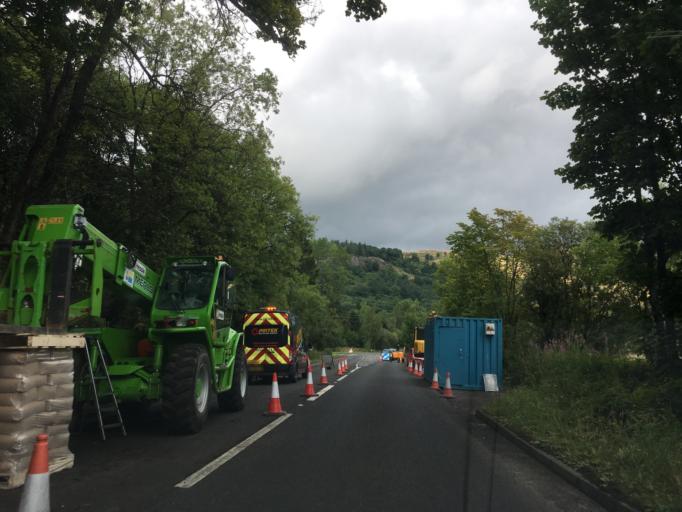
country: GB
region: Scotland
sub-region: Stirling
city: Stirling
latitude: 56.1446
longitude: -3.9074
